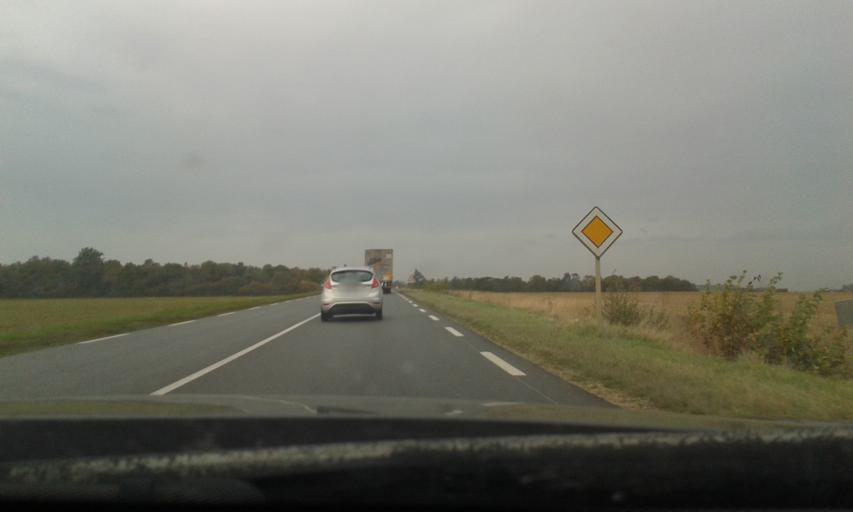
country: FR
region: Centre
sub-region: Departement d'Eure-et-Loir
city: Janville
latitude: 48.2243
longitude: 1.8002
